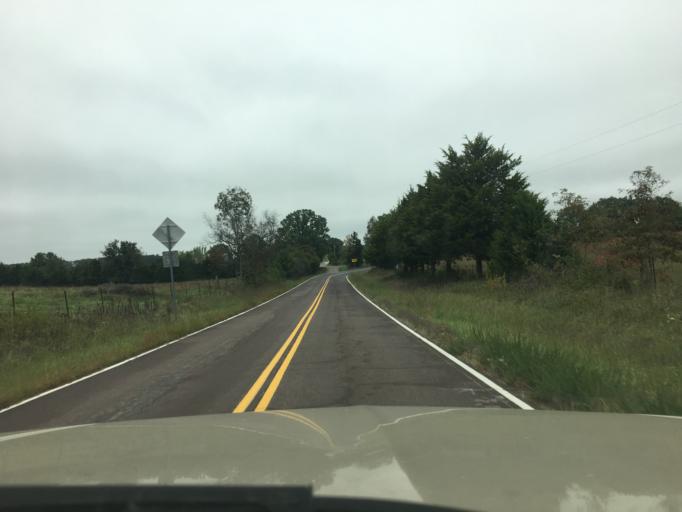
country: US
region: Missouri
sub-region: Crawford County
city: Cuba
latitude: 38.1868
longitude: -91.4848
